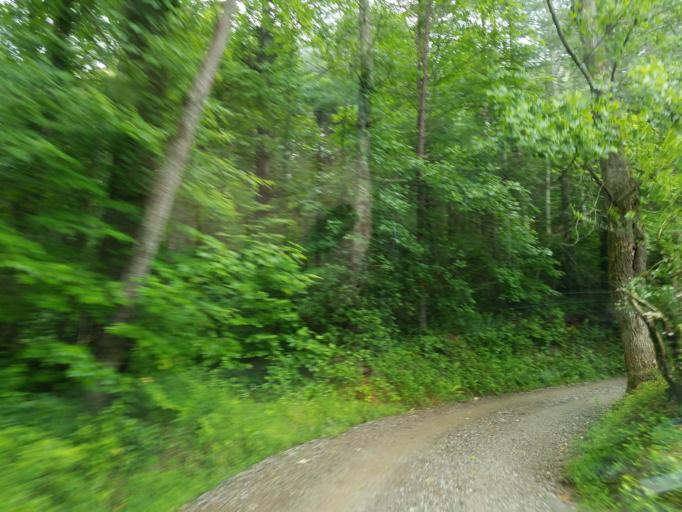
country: US
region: Georgia
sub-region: Lumpkin County
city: Dahlonega
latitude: 34.6929
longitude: -84.0677
